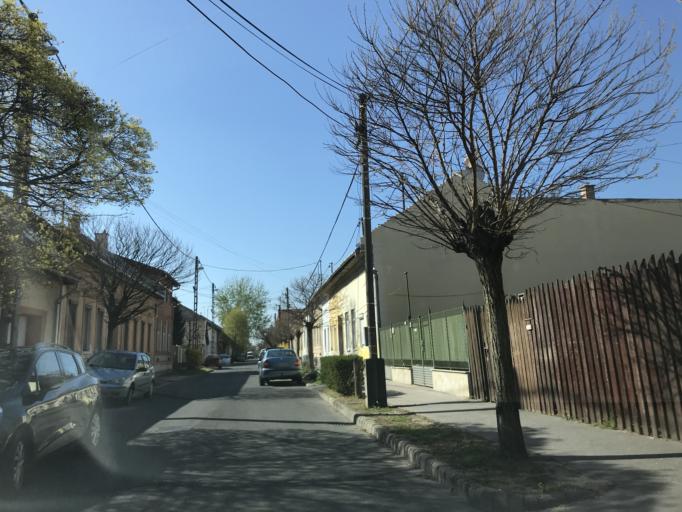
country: HU
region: Budapest
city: Budapest XV. keruelet
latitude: 47.5562
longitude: 19.1162
